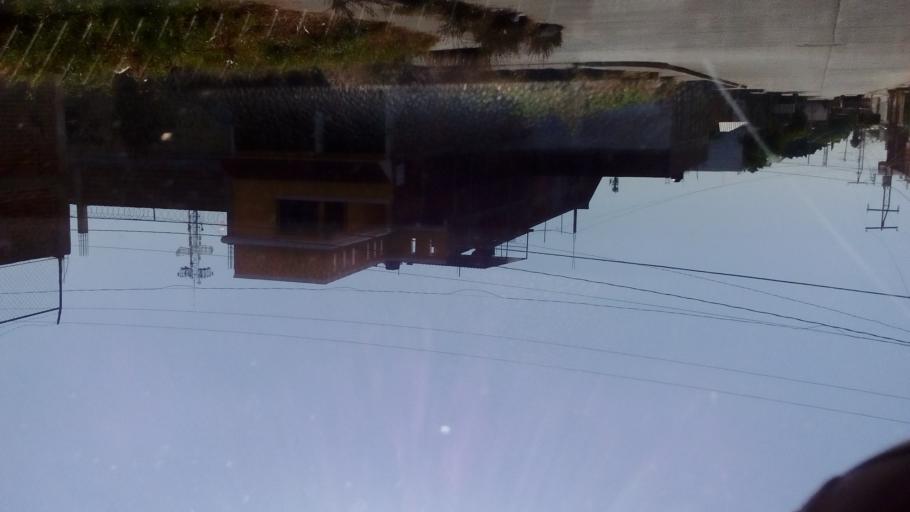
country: MX
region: Guanajuato
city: Leon
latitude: 21.1444
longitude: -101.6775
